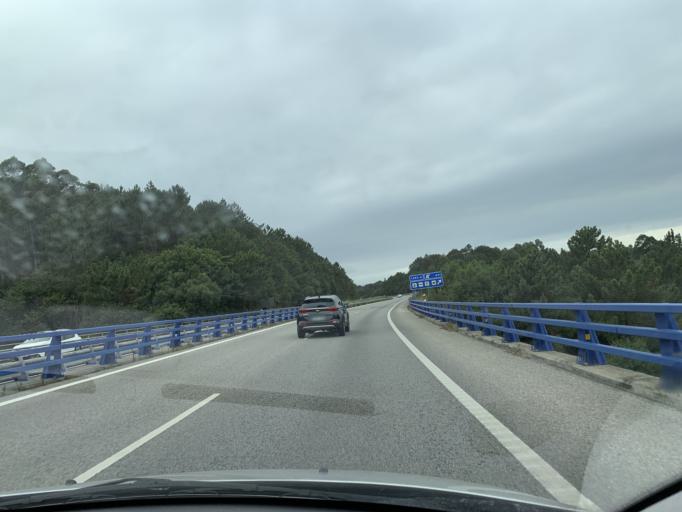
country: ES
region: Asturias
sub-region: Province of Asturias
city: Cudillero
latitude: 43.5599
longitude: -6.2679
